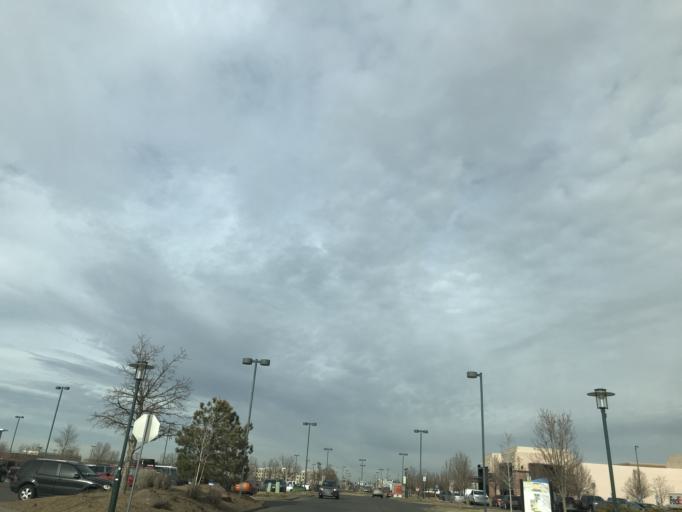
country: US
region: Colorado
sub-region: Adams County
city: Commerce City
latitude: 39.7812
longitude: -104.8933
